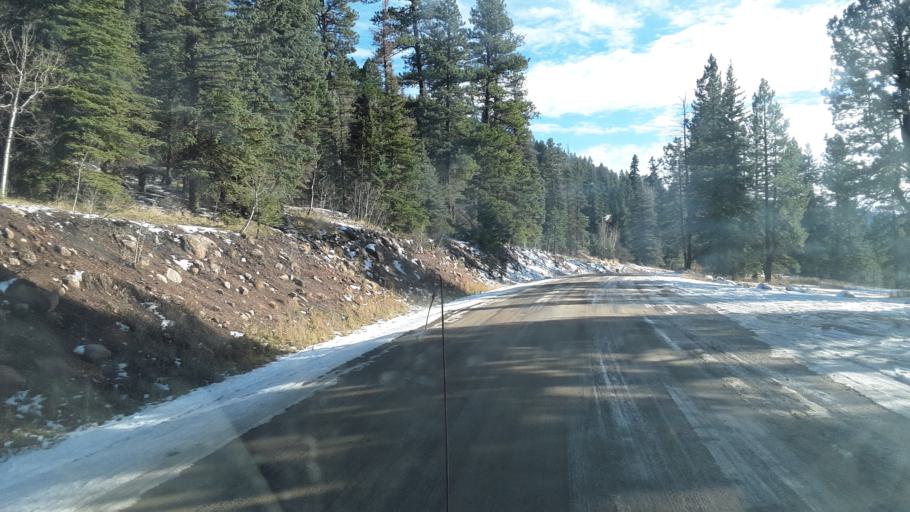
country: US
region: Colorado
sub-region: La Plata County
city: Bayfield
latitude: 37.4050
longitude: -107.6599
